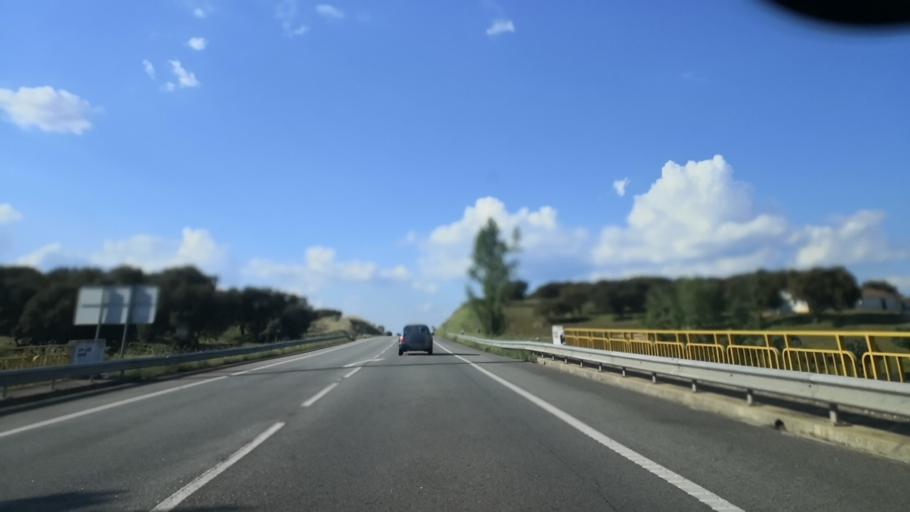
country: PT
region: Portalegre
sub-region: Arronches
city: Arronches
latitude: 39.0683
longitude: -7.4356
